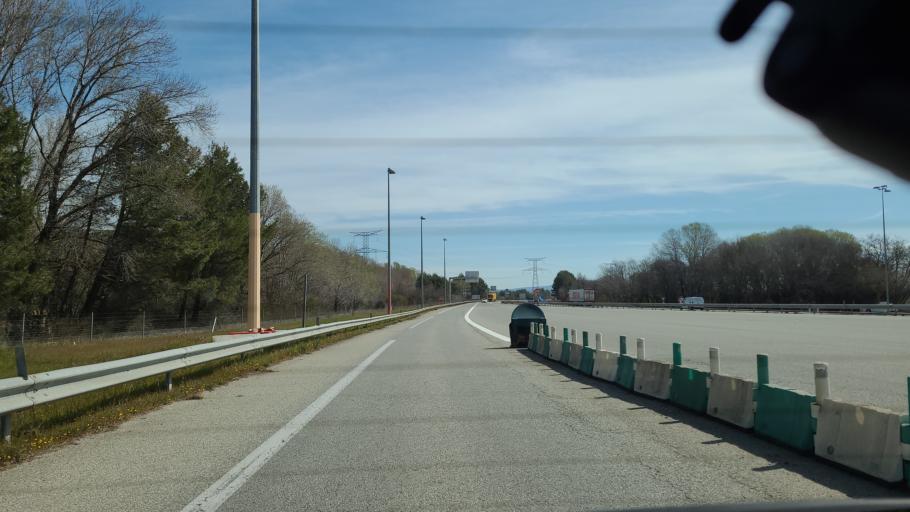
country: FR
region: Provence-Alpes-Cote d'Azur
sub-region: Departement du Vaucluse
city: Pertuis
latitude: 43.6619
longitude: 5.5047
